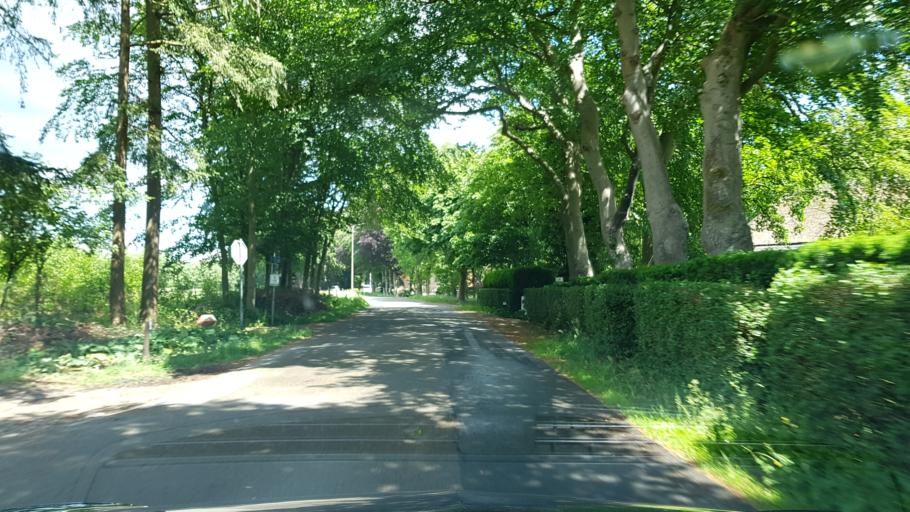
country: NL
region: Gelderland
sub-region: Gemeente Epe
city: Epe
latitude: 52.3504
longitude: 5.9185
